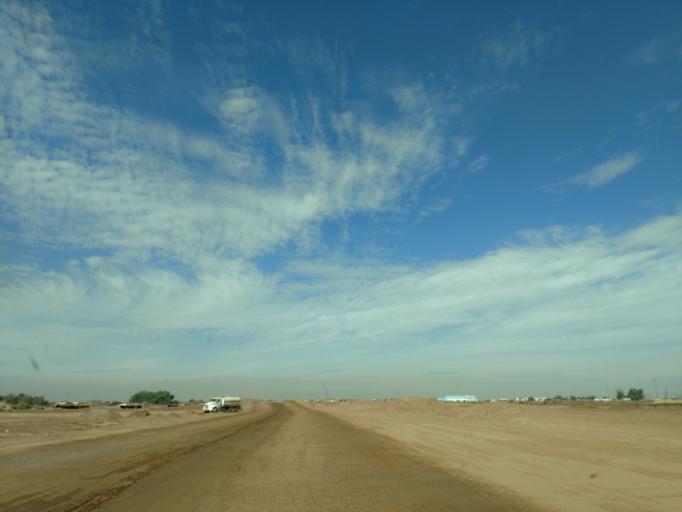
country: US
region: Arizona
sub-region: Maricopa County
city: Laveen
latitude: 33.3831
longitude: -112.1901
